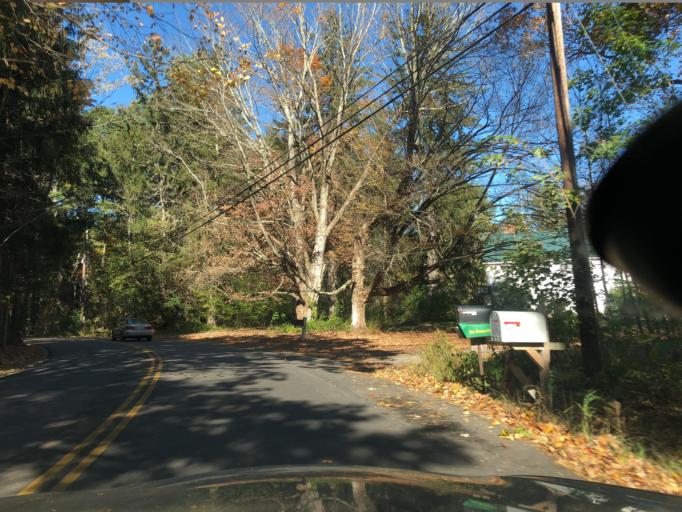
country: US
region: New Hampshire
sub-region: Rockingham County
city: Newmarket
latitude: 43.1116
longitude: -70.9606
